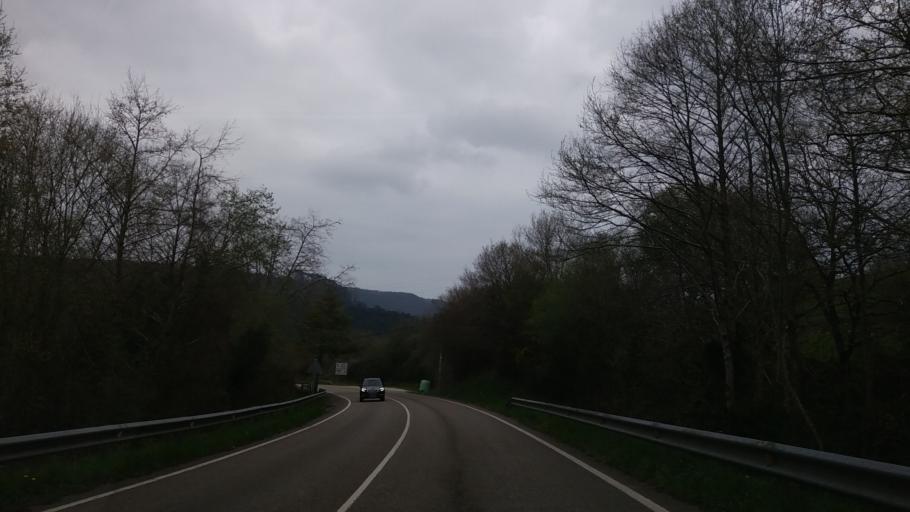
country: ES
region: Cantabria
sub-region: Provincia de Cantabria
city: San Vicente de la Barquera
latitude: 43.3566
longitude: -4.4881
